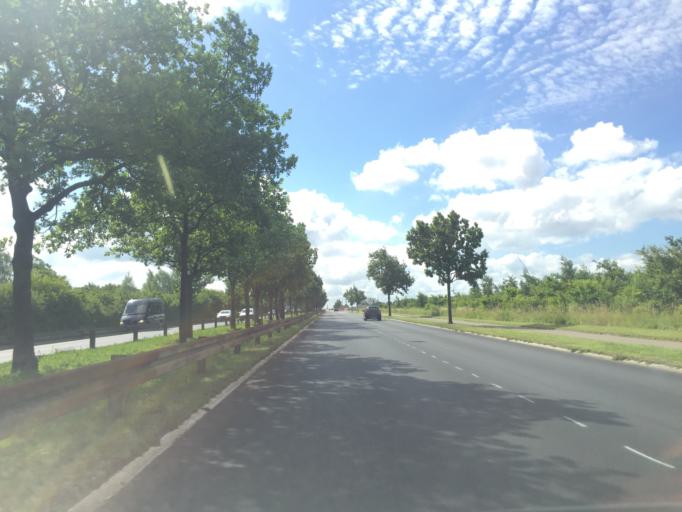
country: DK
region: Capital Region
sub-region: Hvidovre Kommune
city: Hvidovre
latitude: 55.6533
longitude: 12.4561
